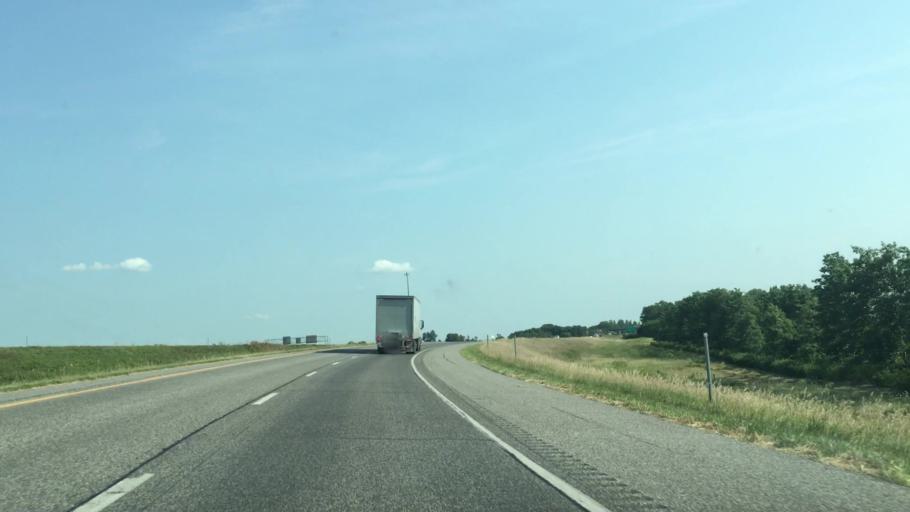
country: US
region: Iowa
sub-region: Scott County
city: Walcott
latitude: 41.6006
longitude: -90.6777
